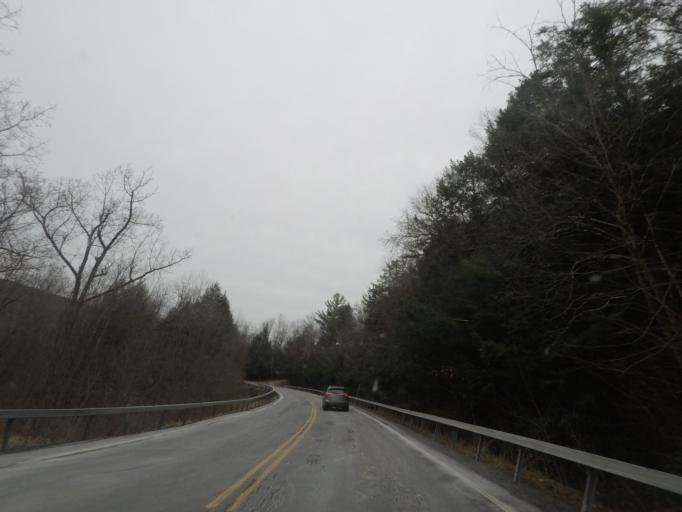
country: US
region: Massachusetts
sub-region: Berkshire County
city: Williamstown
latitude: 42.7434
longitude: -73.3180
